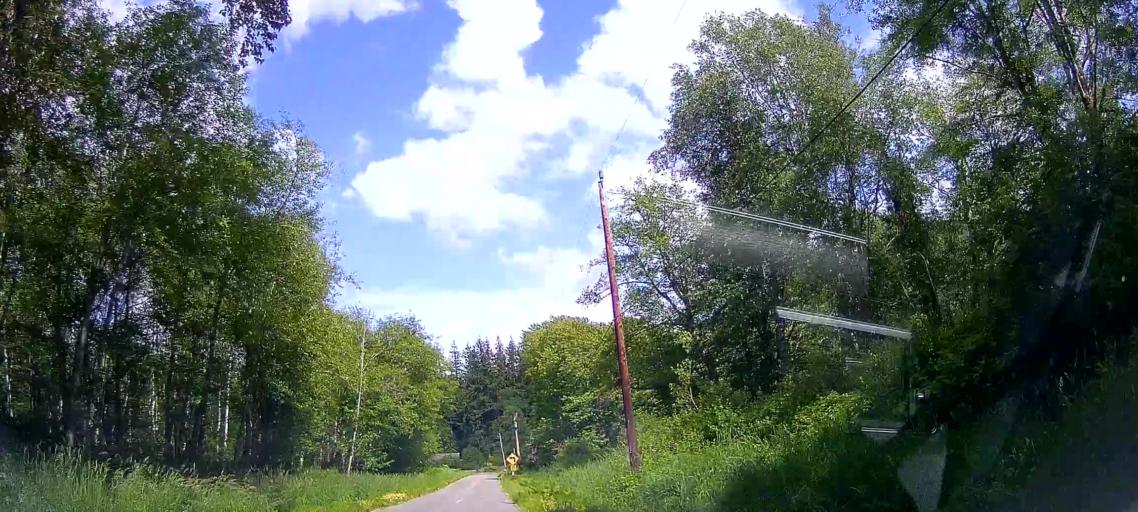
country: US
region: Washington
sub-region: Whatcom County
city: Sudden Valley
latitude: 48.6603
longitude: -122.2002
